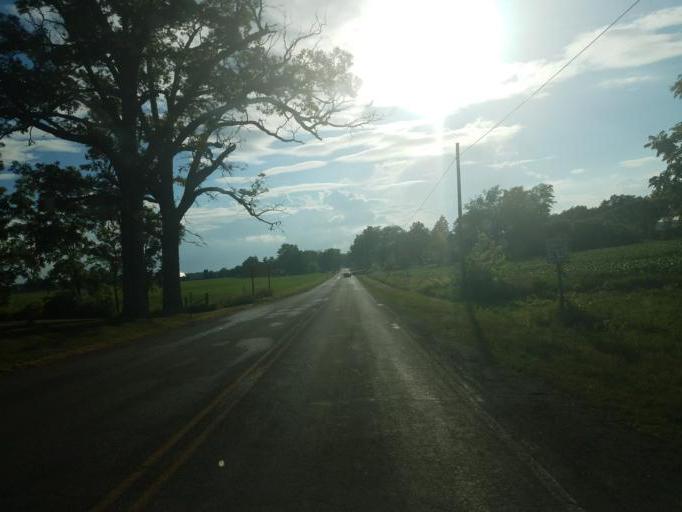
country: US
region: Indiana
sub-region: Steuben County
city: Fremont
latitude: 41.7967
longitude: -84.9986
